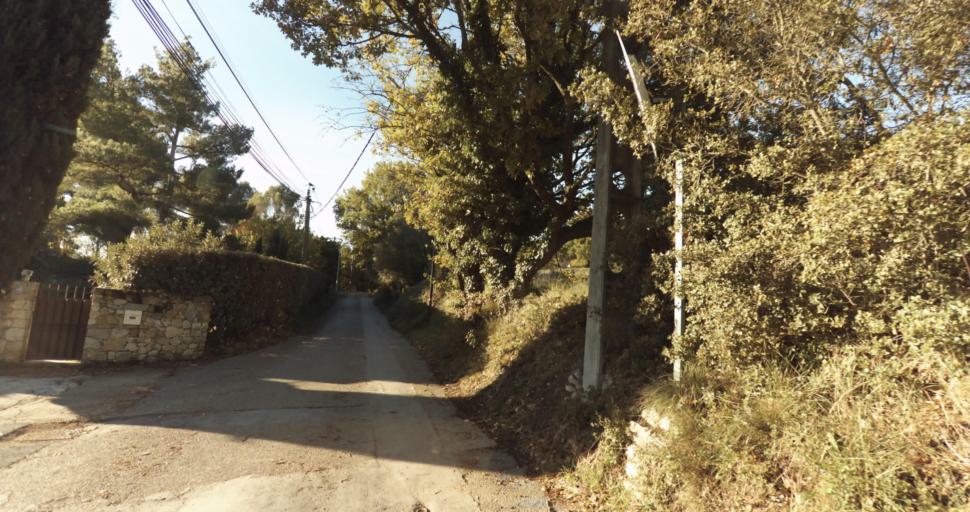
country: FR
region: Provence-Alpes-Cote d'Azur
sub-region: Departement des Bouches-du-Rhone
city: Venelles
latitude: 43.6069
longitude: 5.4817
